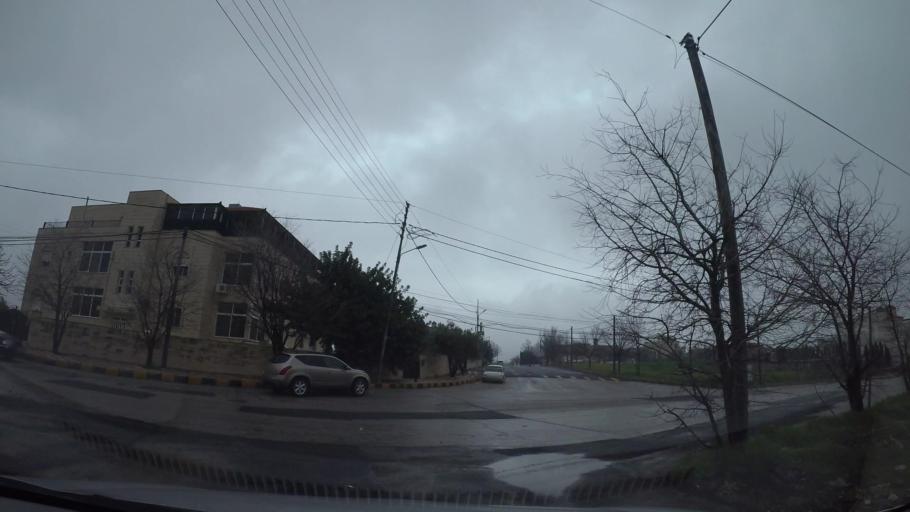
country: JO
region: Amman
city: Al Jubayhah
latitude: 32.0105
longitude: 35.8260
